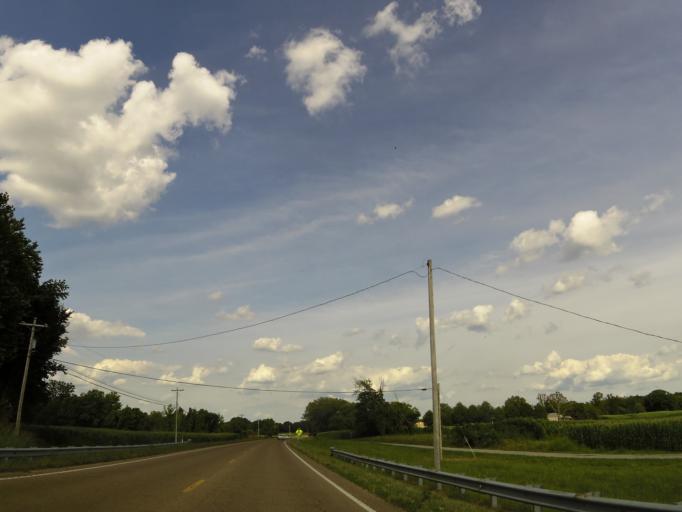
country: US
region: Tennessee
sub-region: Carroll County
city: Bruceton
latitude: 36.0380
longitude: -88.3089
